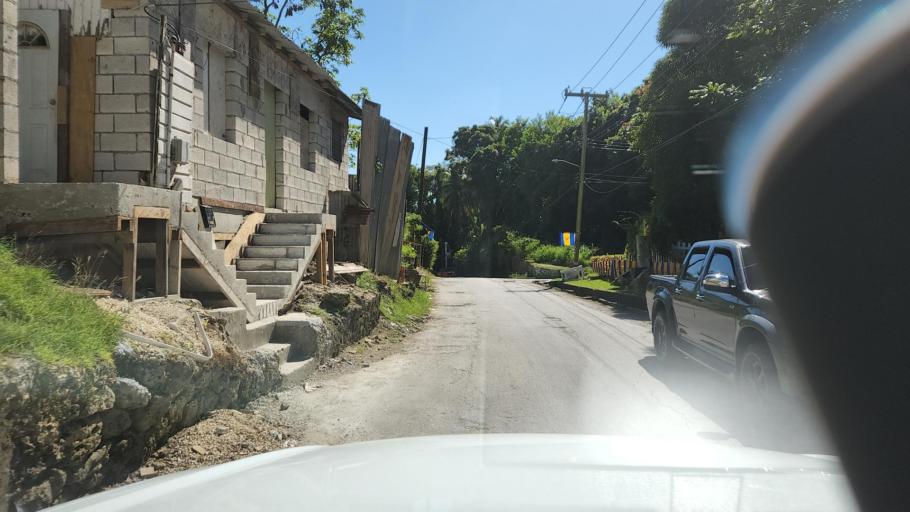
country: BB
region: Saint Thomas
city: Welchman Hall
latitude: 13.1932
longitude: -59.5954
